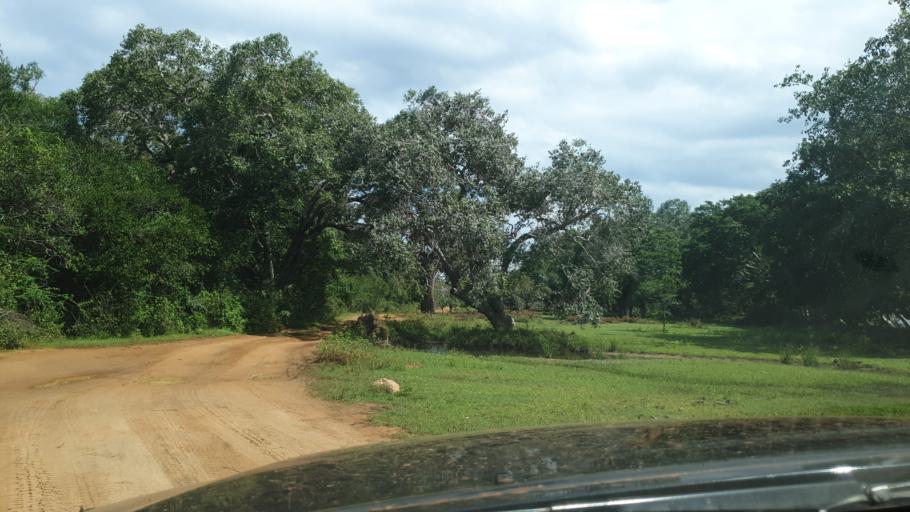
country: LK
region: North Central
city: Anuradhapura
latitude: 8.4223
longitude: 80.0058
